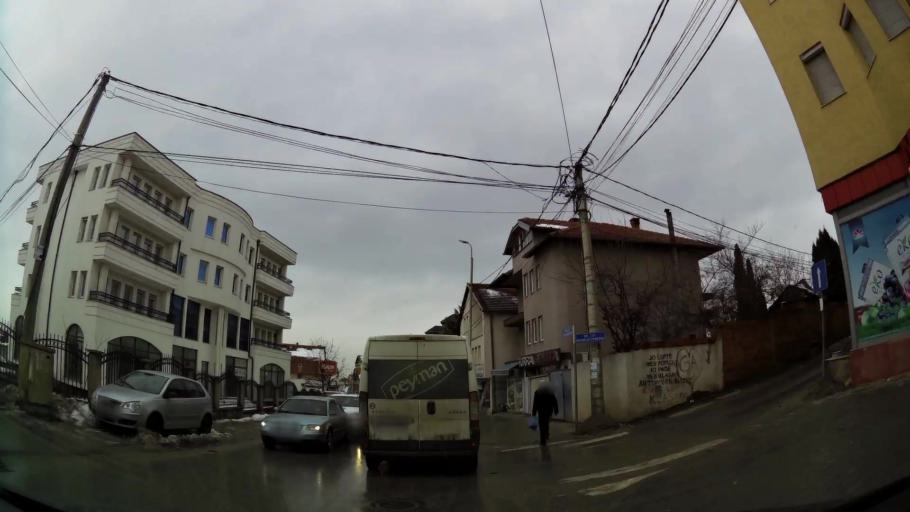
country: XK
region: Pristina
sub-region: Komuna e Prishtines
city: Pristina
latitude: 42.6590
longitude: 21.1823
